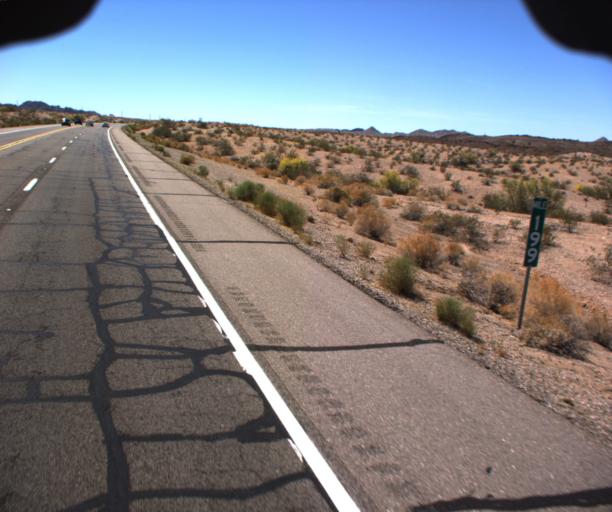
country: US
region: Arizona
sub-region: Mohave County
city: Desert Hills
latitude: 34.6887
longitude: -114.3026
